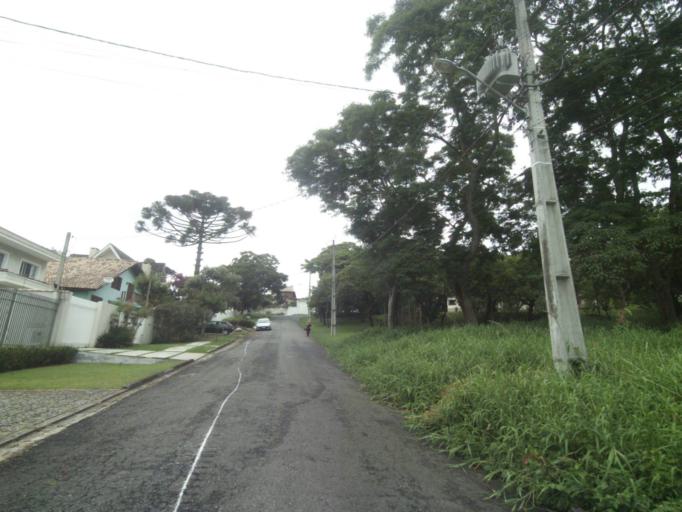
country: BR
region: Parana
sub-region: Curitiba
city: Curitiba
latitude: -25.4088
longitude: -49.2875
